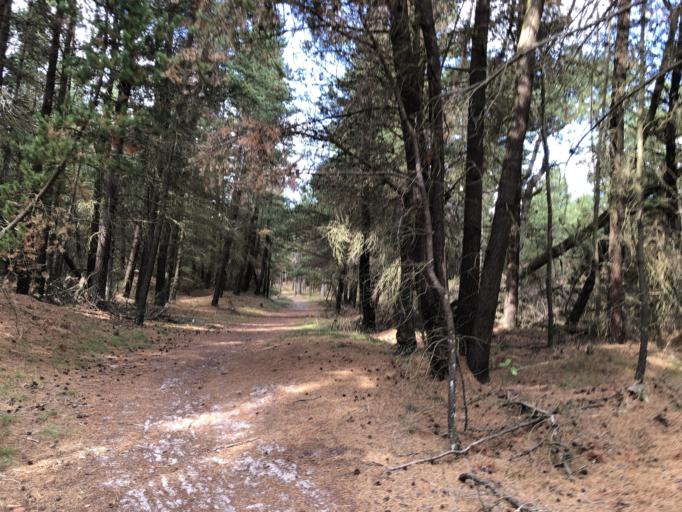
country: DK
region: Central Jutland
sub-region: Holstebro Kommune
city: Ulfborg
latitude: 56.2856
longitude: 8.1570
